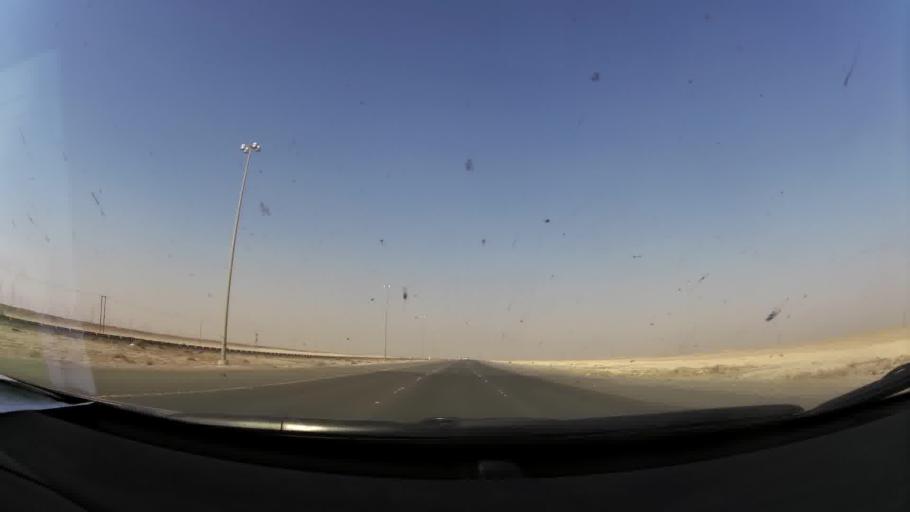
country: KW
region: Muhafazat al Jahra'
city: Al Jahra'
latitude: 29.6320
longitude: 47.6643
